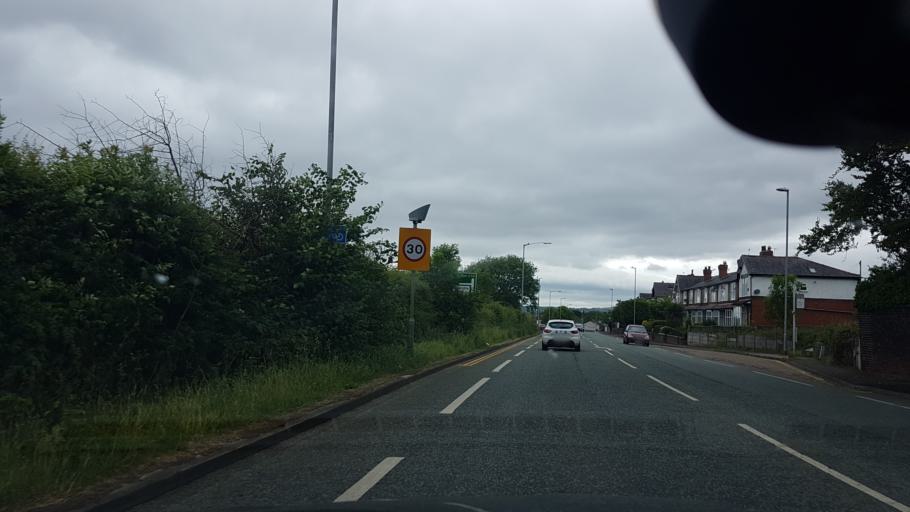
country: GB
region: England
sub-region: Borough of Bolton
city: Little Lever
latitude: 53.5773
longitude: -2.3653
